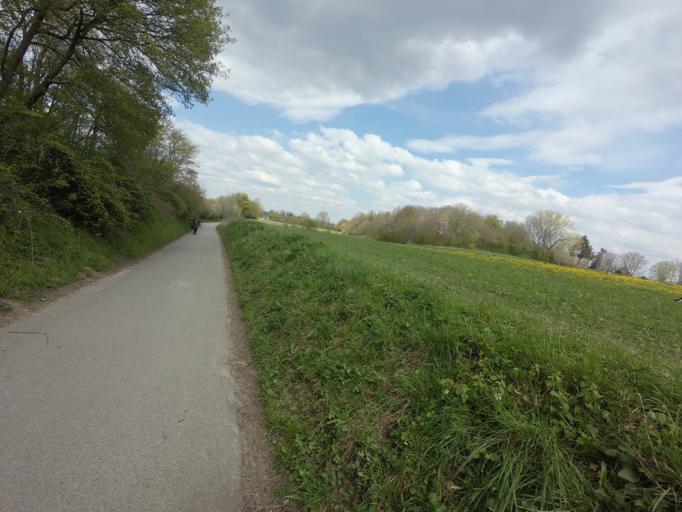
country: NL
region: Limburg
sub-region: Gemeente Maastricht
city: Maastricht
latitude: 50.8285
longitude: 5.6860
